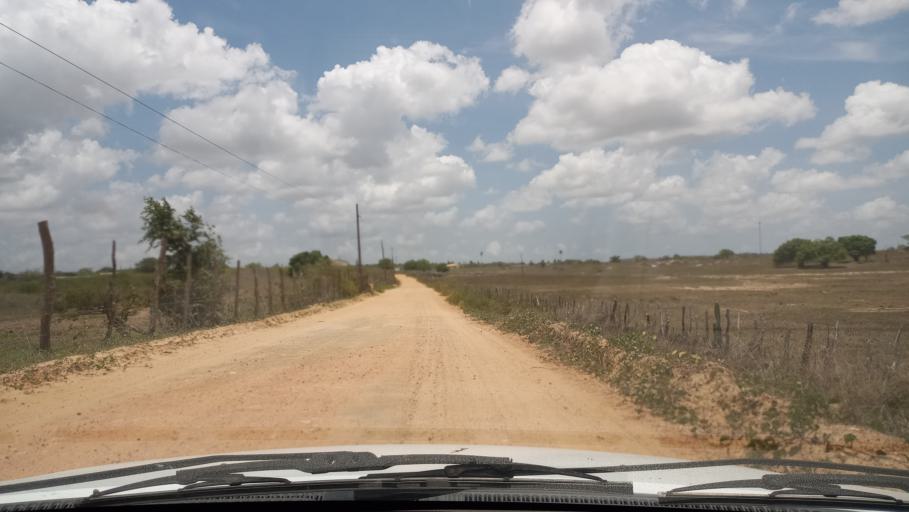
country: BR
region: Rio Grande do Norte
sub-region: Brejinho
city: Brejinho
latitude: -6.2786
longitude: -35.3347
